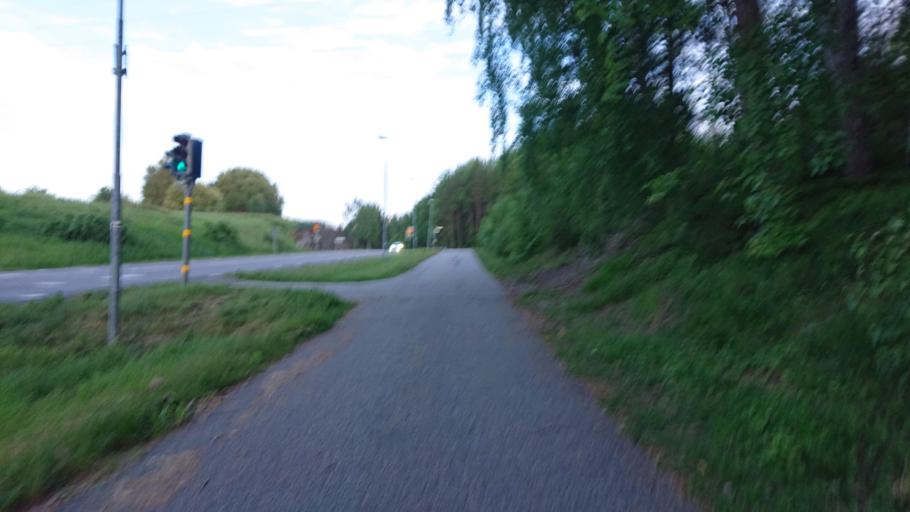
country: SE
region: Stockholm
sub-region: Osterakers Kommun
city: Akersberga
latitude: 59.4990
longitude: 18.3159
